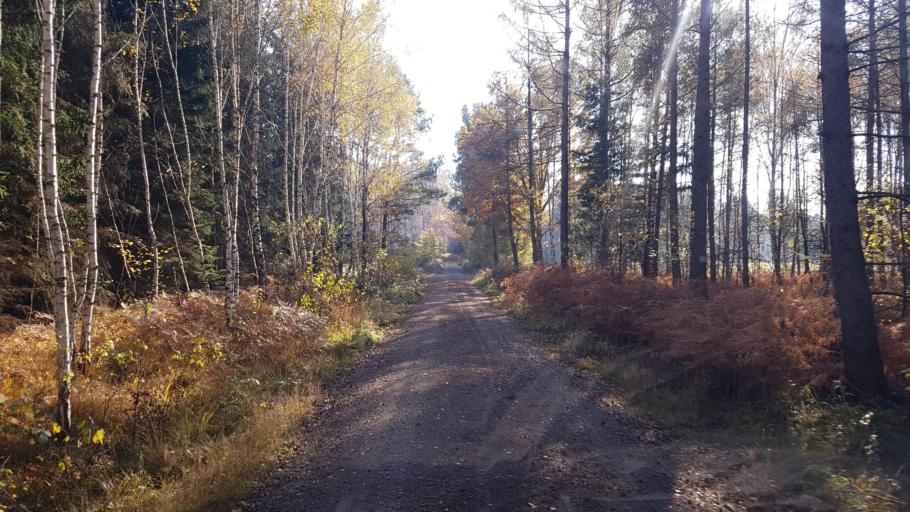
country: DE
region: Brandenburg
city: Ruckersdorf
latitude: 51.5649
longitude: 13.6206
